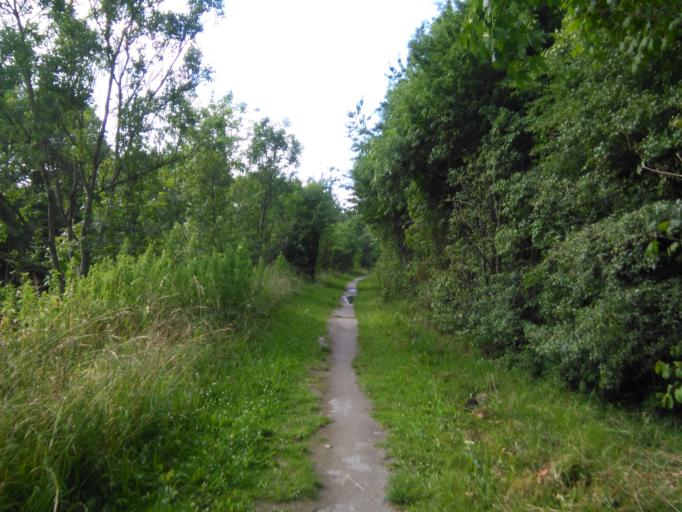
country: DK
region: Central Jutland
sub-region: Horsens Kommune
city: Braedstrup
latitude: 55.9749
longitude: 9.7025
